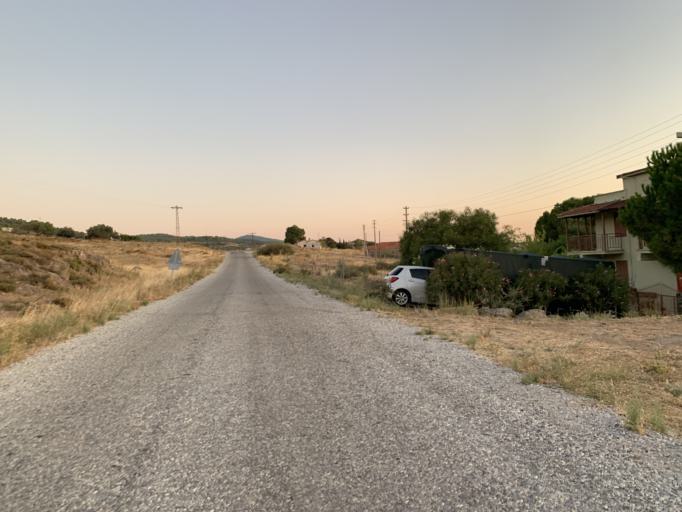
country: TR
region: Izmir
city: Uzunkuyu
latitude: 38.3256
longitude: 26.5835
